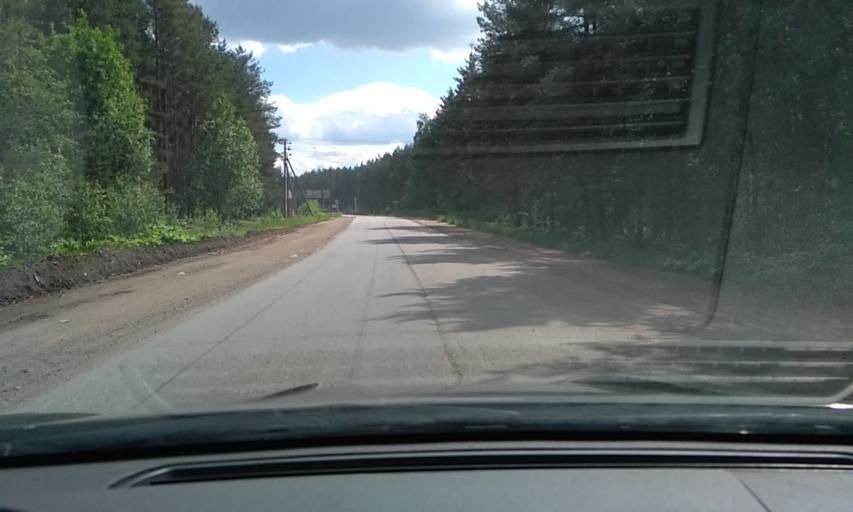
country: RU
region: Leningrad
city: Imeni Sverdlova
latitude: 59.8581
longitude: 30.6720
